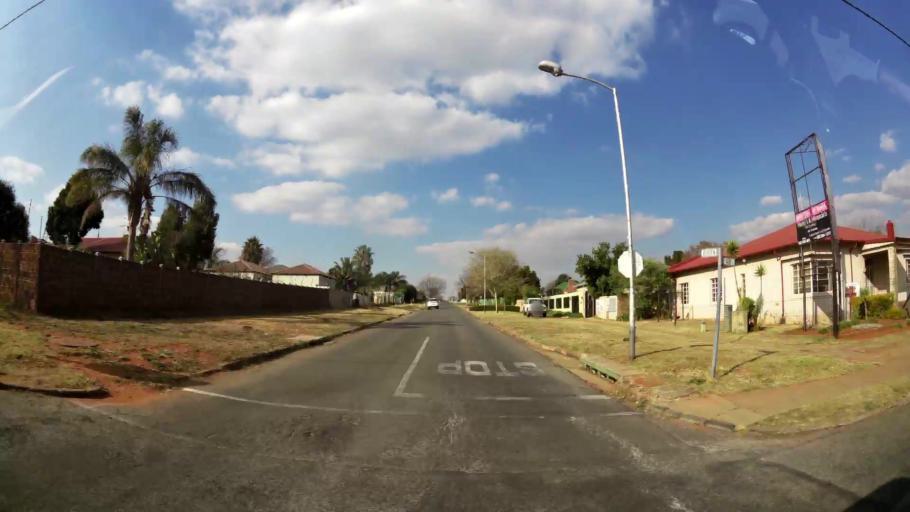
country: ZA
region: Gauteng
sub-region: West Rand District Municipality
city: Krugersdorp
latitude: -26.0897
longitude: 27.7684
